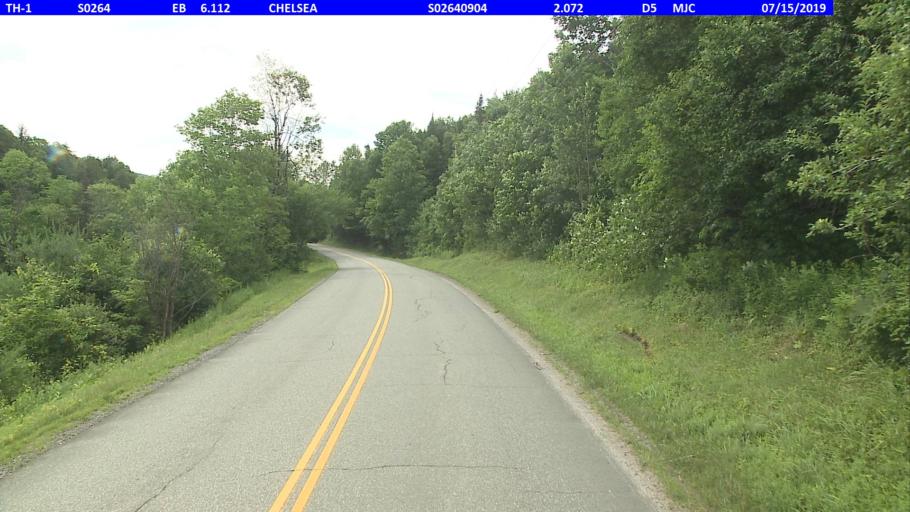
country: US
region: Vermont
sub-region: Orange County
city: Chelsea
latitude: 43.9678
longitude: -72.4771
